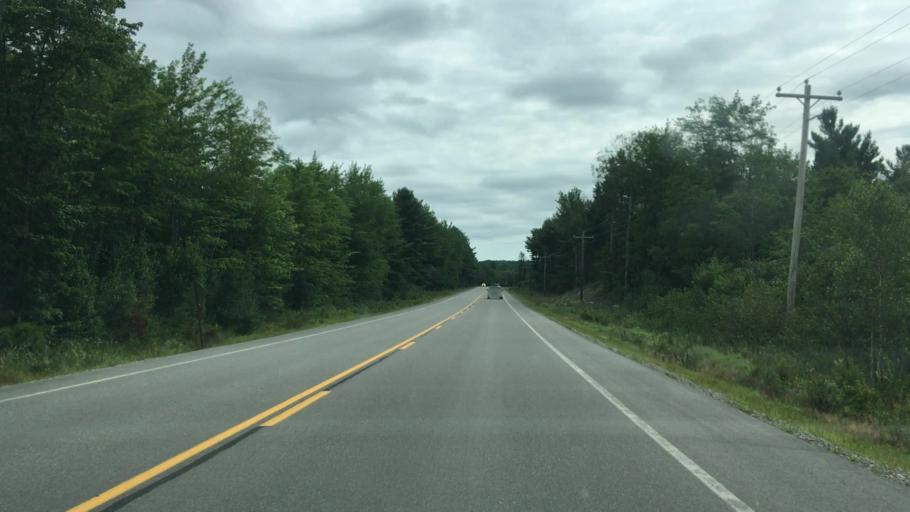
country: US
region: Maine
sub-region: Washington County
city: Machias
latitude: 45.0012
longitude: -67.5791
